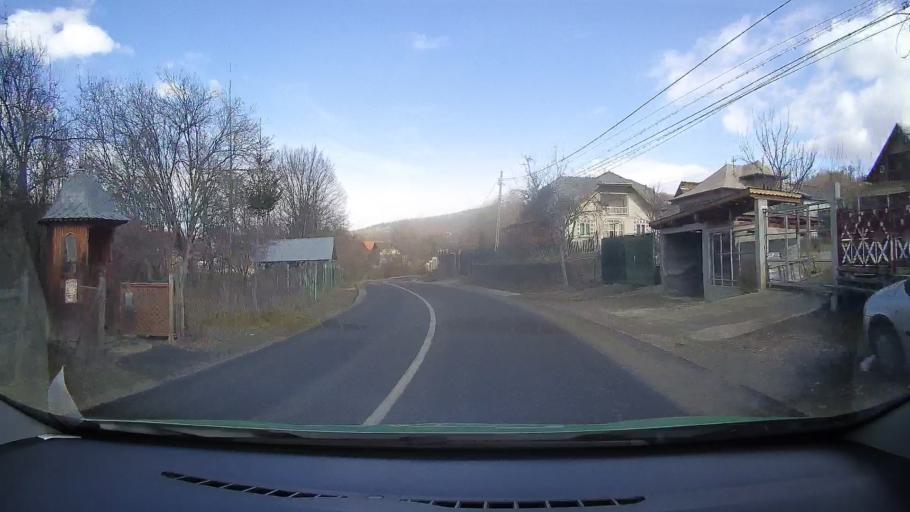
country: RO
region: Dambovita
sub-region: Comuna Runcu
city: Badeni
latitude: 45.1405
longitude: 25.4026
